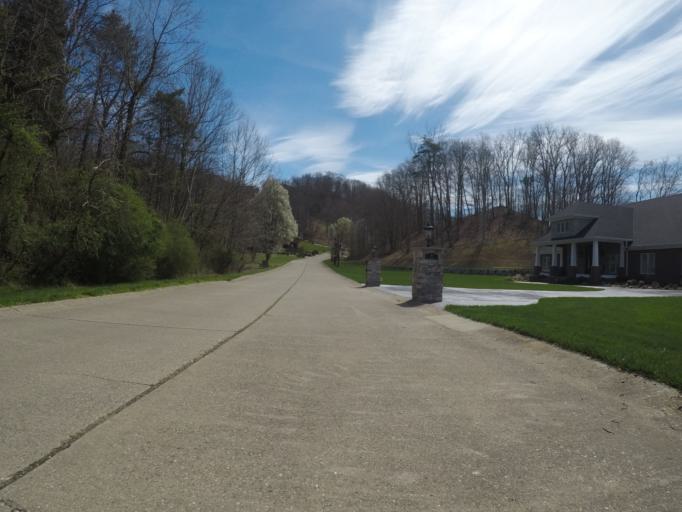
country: US
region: West Virginia
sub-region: Cabell County
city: Pea Ridge
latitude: 38.4057
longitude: -82.3135
